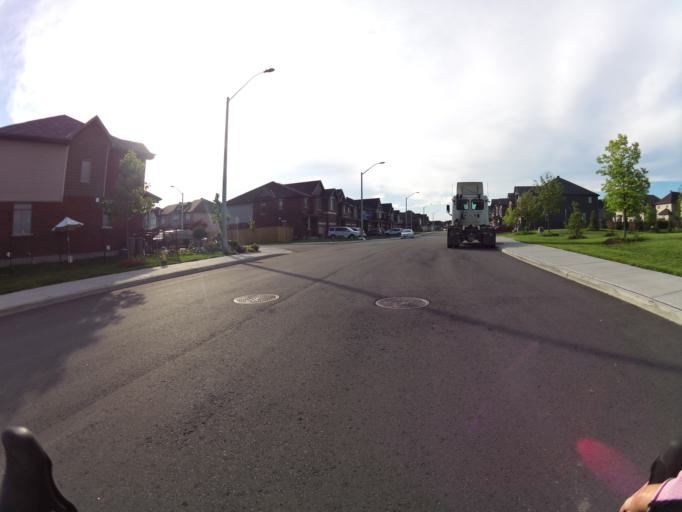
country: CA
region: Ontario
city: Bells Corners
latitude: 45.2718
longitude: -75.7811
